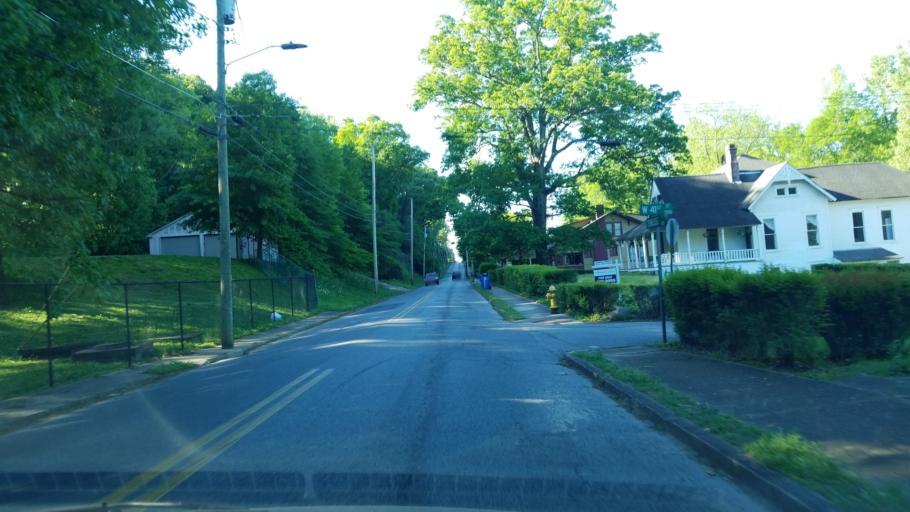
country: US
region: Tennessee
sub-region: Hamilton County
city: Lookout Mountain
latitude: 35.0069
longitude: -85.3274
